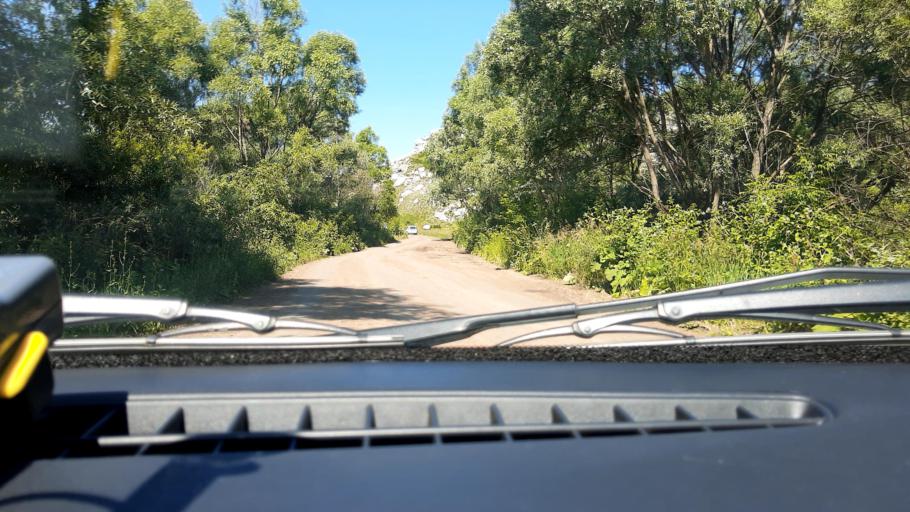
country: RU
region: Bashkortostan
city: Karmaskaly
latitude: 54.3585
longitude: 55.9027
